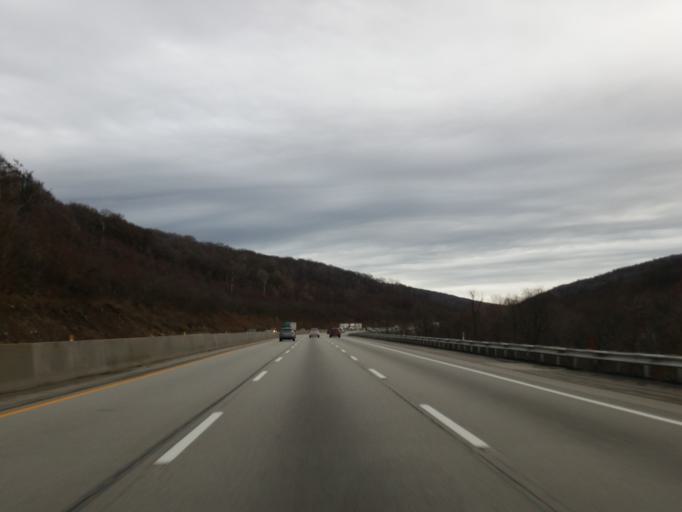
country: US
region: Pennsylvania
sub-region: Westmoreland County
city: Ligonier
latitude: 40.1180
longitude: -79.2668
